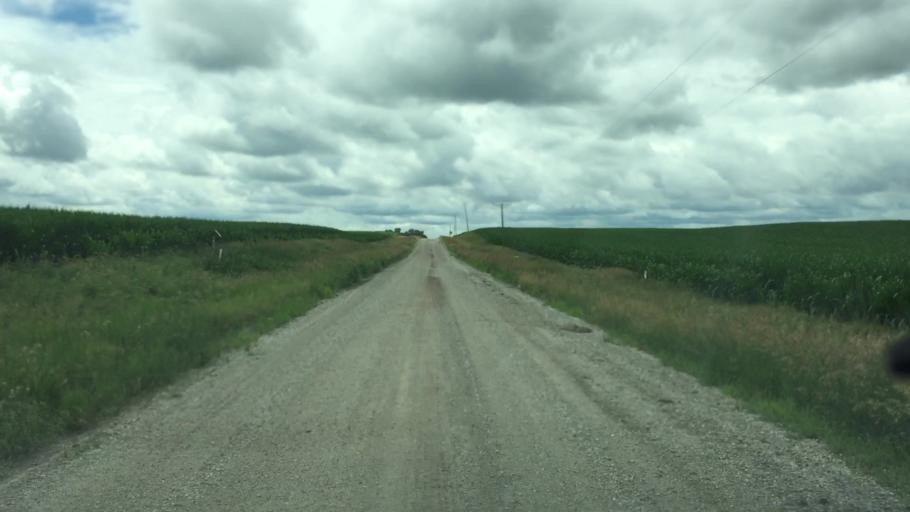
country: US
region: Iowa
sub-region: Jasper County
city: Prairie City
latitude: 41.5853
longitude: -93.1596
